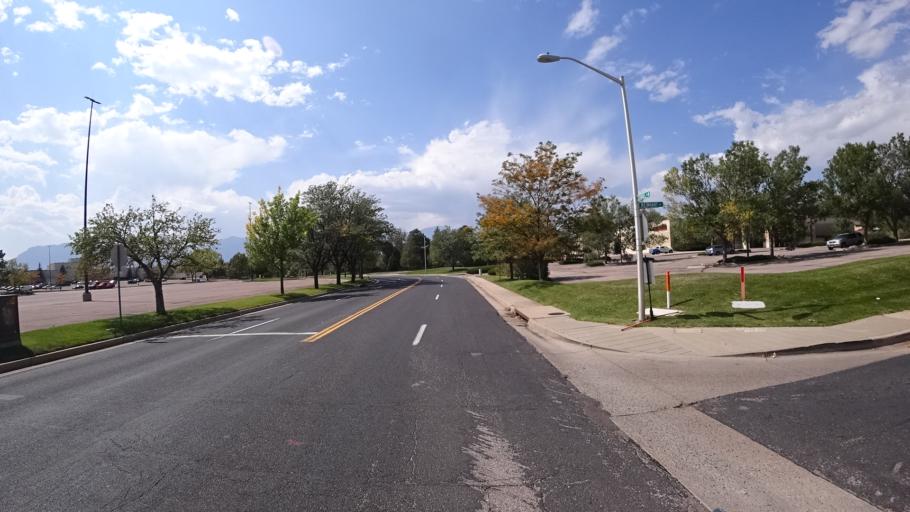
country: US
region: Colorado
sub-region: El Paso County
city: Colorado Springs
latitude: 38.8459
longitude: -104.7626
